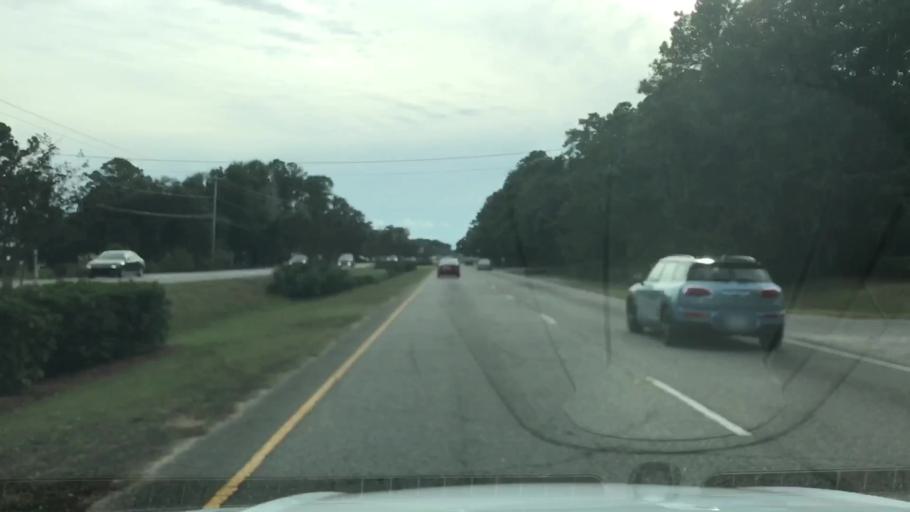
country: US
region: South Carolina
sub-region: Georgetown County
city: Murrells Inlet
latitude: 33.4635
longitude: -79.1103
